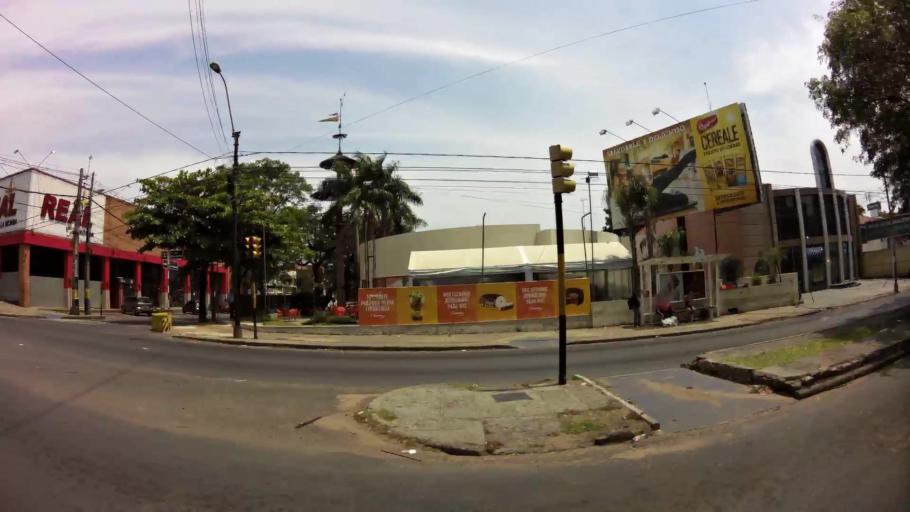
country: PY
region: Central
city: Lambare
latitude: -25.2968
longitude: -57.5780
